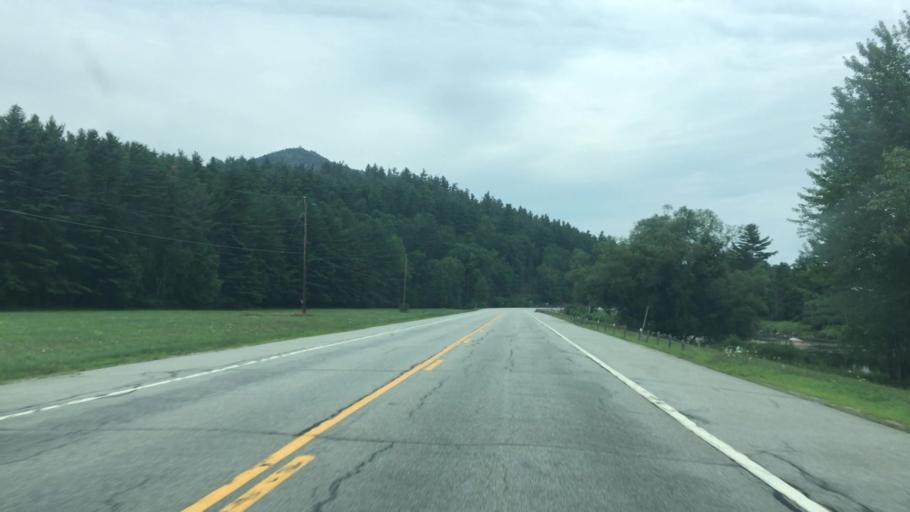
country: US
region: New York
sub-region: Essex County
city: Elizabethtown
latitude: 44.3509
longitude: -73.7559
